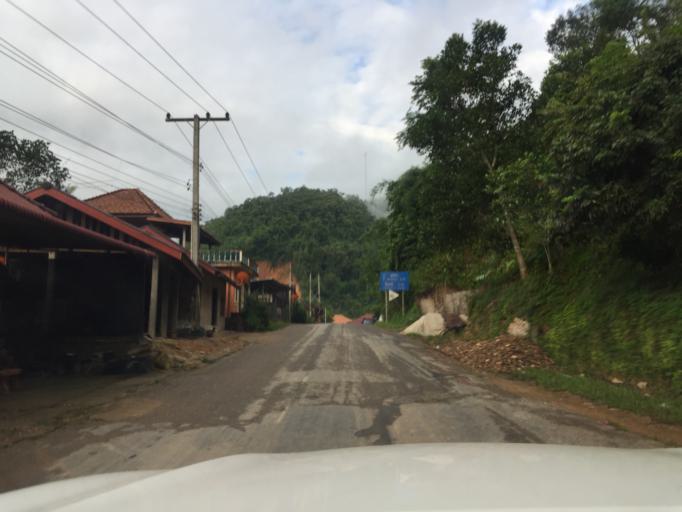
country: LA
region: Phongsali
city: Khoa
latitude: 21.1026
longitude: 102.2551
